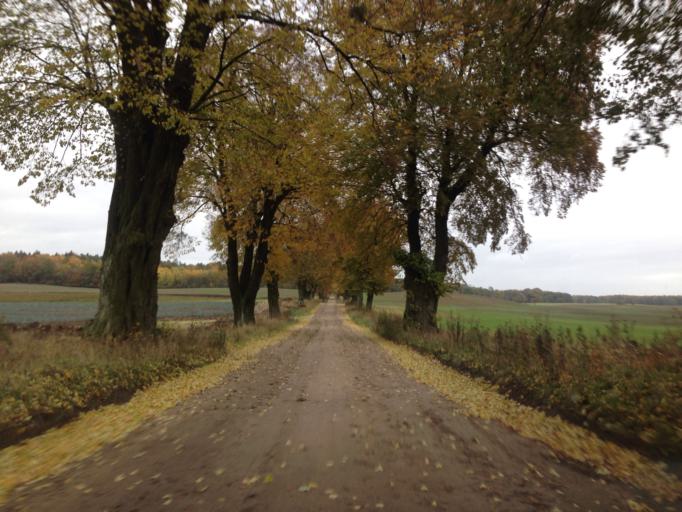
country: PL
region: Warmian-Masurian Voivodeship
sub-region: Powiat ilawski
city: Susz
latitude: 53.6743
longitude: 19.2919
